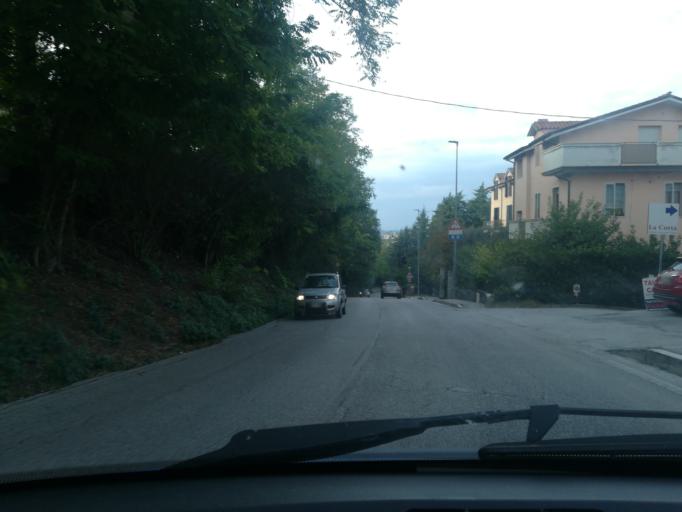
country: IT
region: The Marches
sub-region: Provincia di Macerata
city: Villa Potenza
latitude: 43.3089
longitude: 13.4374
